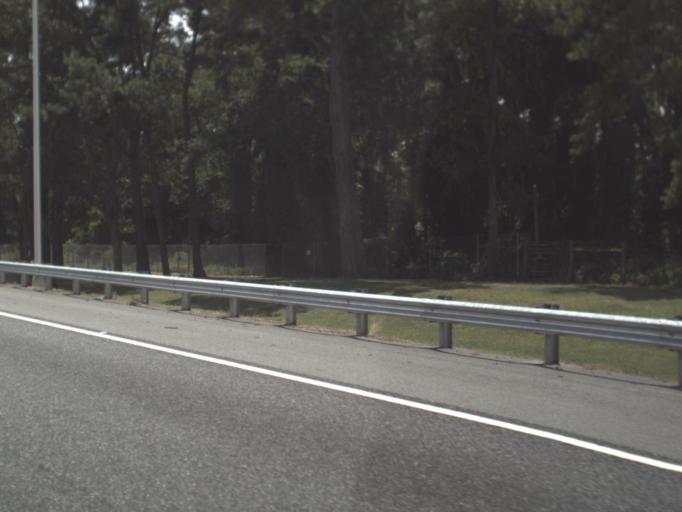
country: US
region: Florida
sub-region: Alachua County
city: High Springs
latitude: 29.9823
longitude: -82.5803
